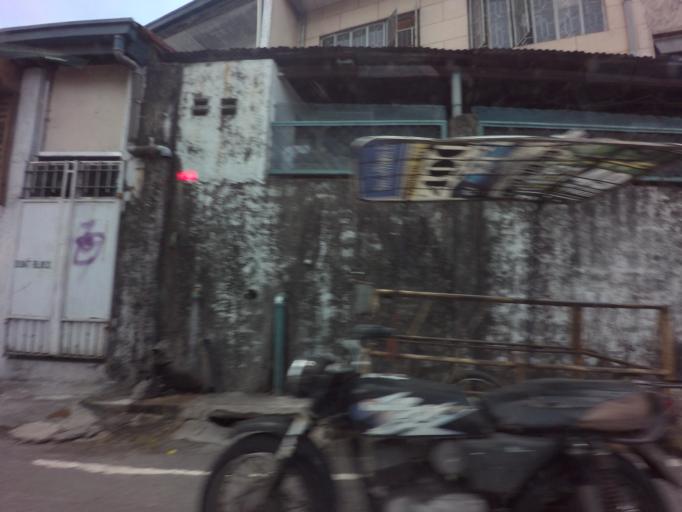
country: PH
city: Sambayanihan People's Village
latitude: 14.4296
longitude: 121.0146
